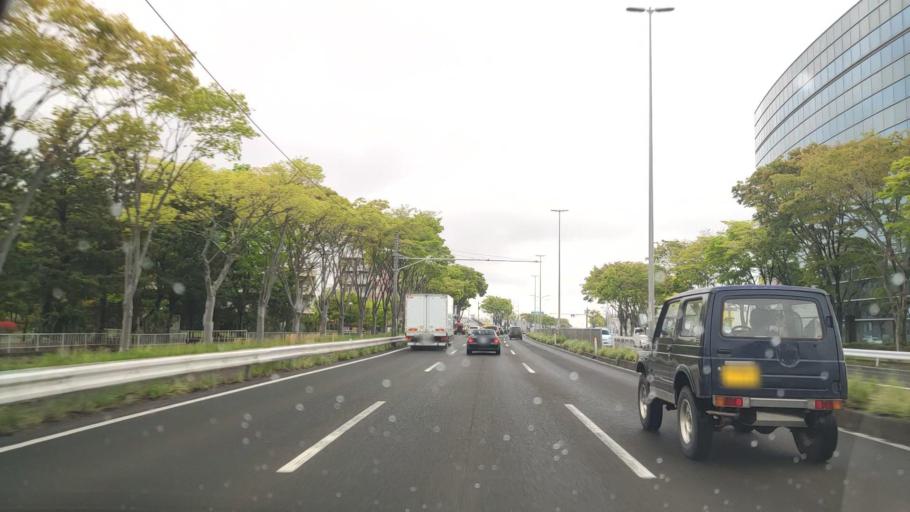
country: JP
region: Miyagi
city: Sendai
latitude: 38.2318
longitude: 140.9074
